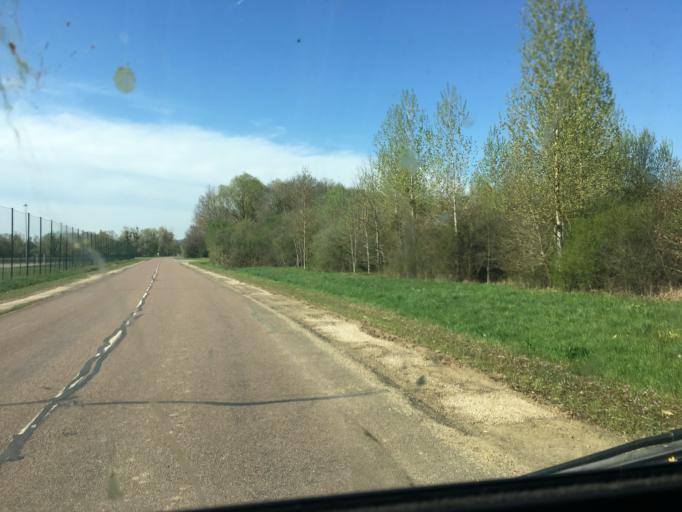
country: FR
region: Lorraine
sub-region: Departement de la Meuse
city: Vigneulles-les-Hattonchatel
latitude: 48.9410
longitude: 5.7129
